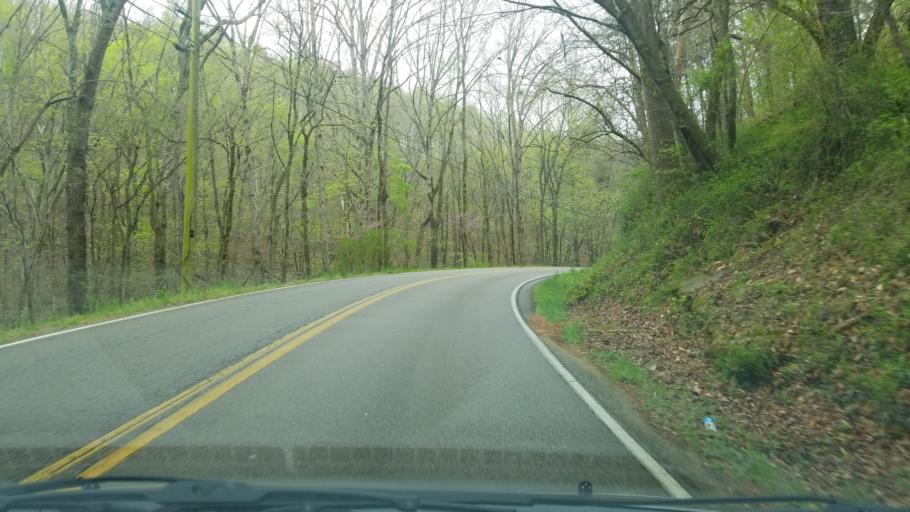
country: US
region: Tennessee
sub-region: Hamilton County
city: Collegedale
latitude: 35.0098
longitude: -85.0748
